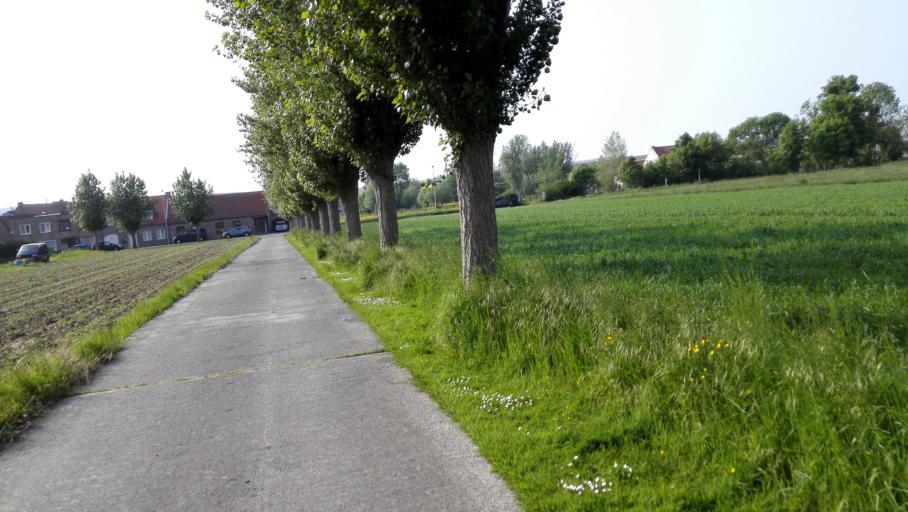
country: BE
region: Flanders
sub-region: Provincie West-Vlaanderen
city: Zeebrugge
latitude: 51.3097
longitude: 3.1991
